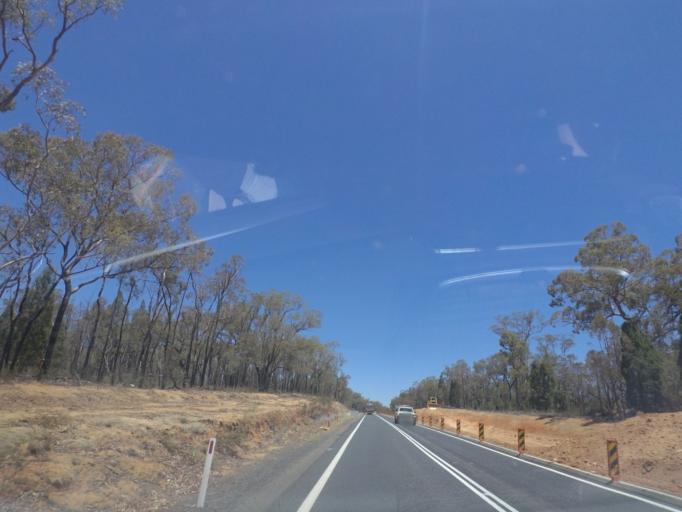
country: AU
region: New South Wales
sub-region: Warrumbungle Shire
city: Coonabarabran
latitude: -30.9227
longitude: 149.4321
